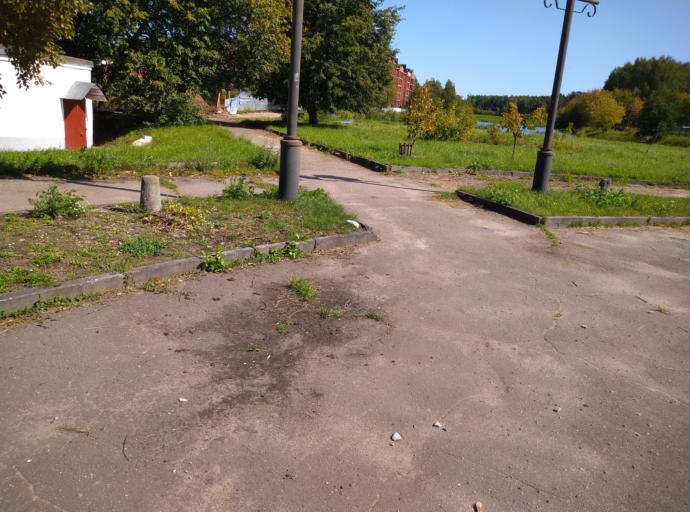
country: RU
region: Kostroma
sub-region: Kostromskoy Rayon
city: Kostroma
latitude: 57.7985
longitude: 40.9534
